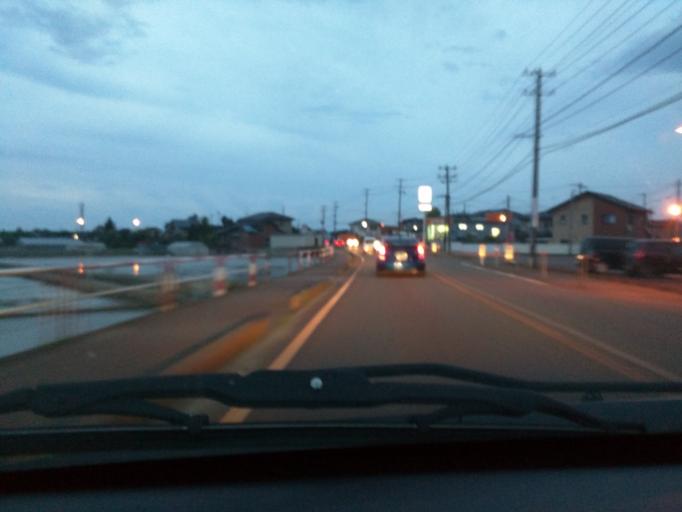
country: JP
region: Niigata
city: Kashiwazaki
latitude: 37.3570
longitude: 138.5959
